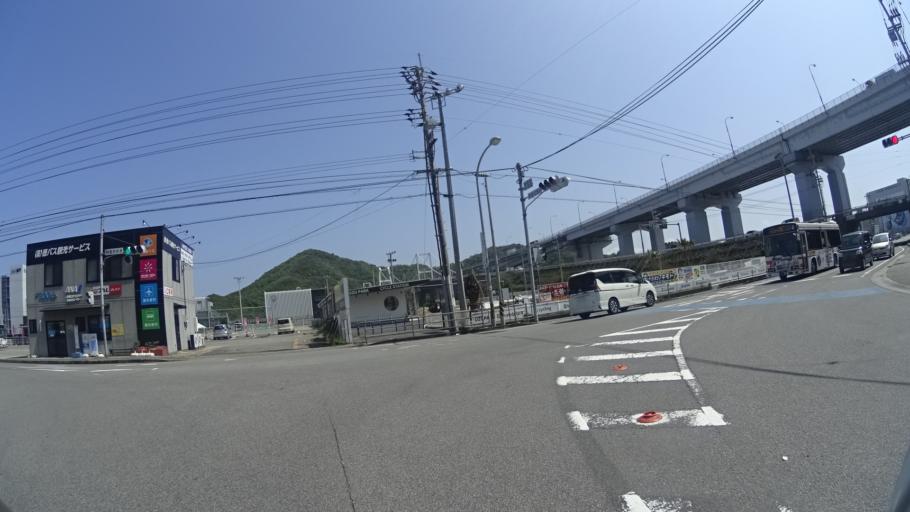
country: JP
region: Tokushima
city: Narutocho-mitsuishi
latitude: 34.1892
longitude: 134.6100
